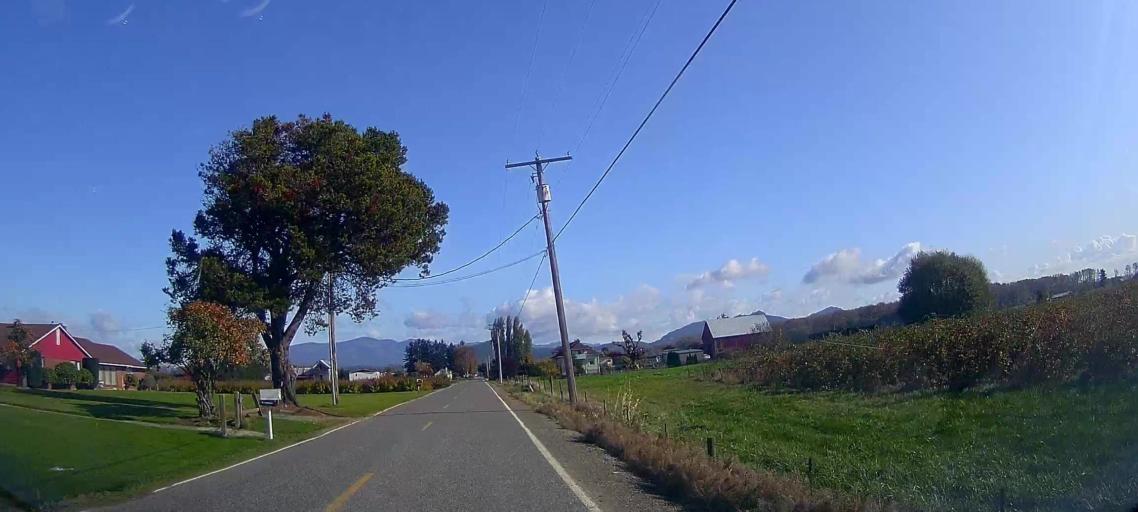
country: US
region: Washington
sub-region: Skagit County
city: Mount Vernon
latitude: 48.3992
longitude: -122.3893
